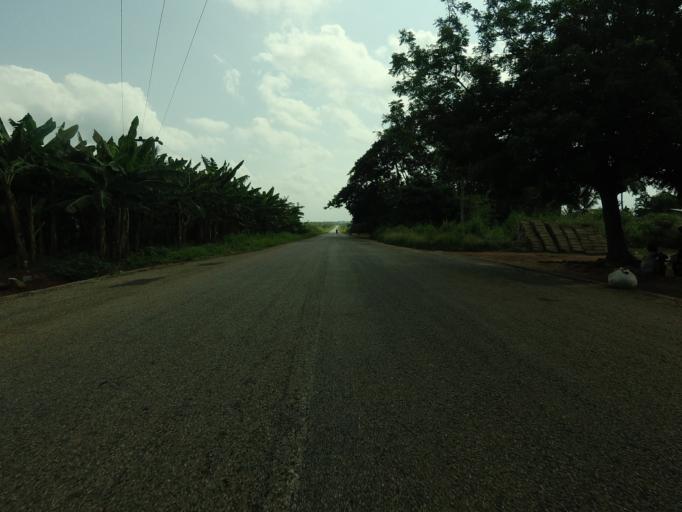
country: TG
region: Maritime
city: Tsevie
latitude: 6.3921
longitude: 0.8328
